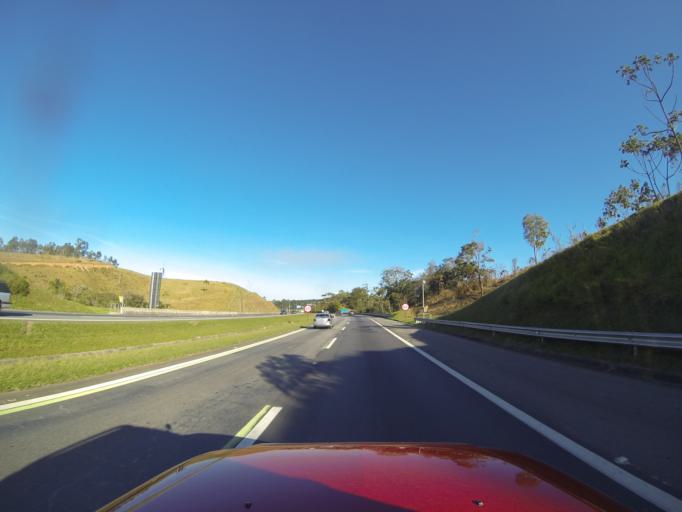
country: BR
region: Sao Paulo
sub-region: Santa Isabel
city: Santa Isabel
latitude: -23.1961
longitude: -46.1850
